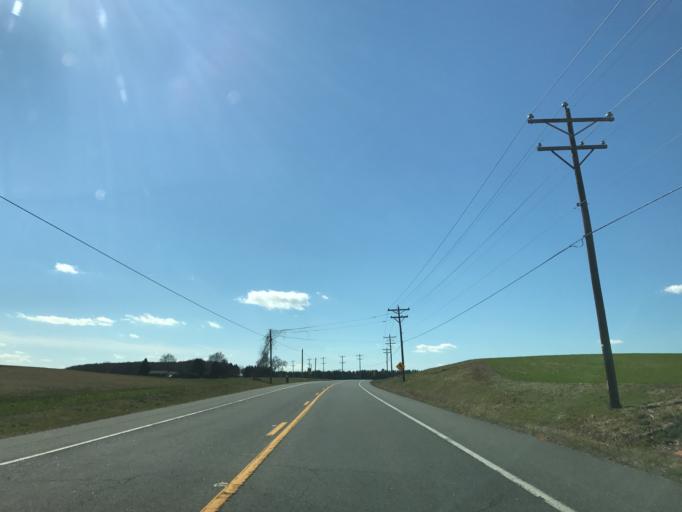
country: US
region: Maryland
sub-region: Kent County
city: Chestertown
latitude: 39.2172
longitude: -76.0873
